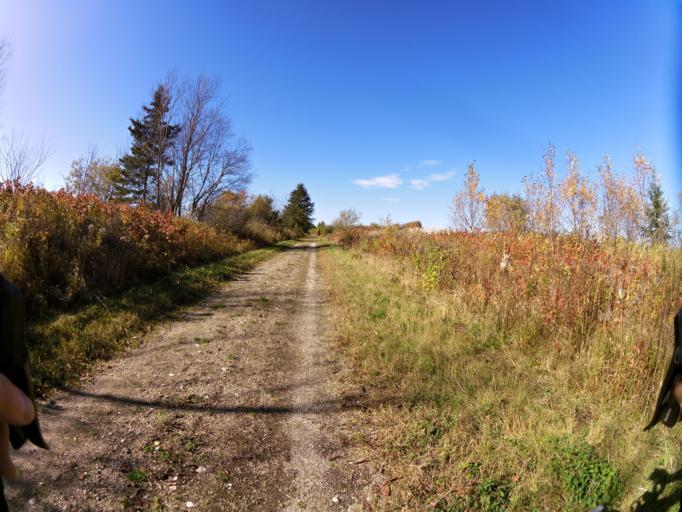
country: CA
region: Quebec
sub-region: Outaouais
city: Wakefield
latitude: 45.8654
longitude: -76.0146
